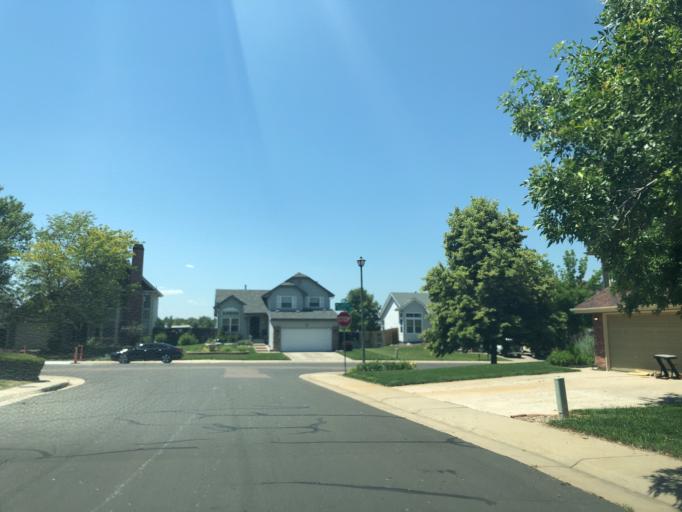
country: US
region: Colorado
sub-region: Arapahoe County
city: Dove Valley
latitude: 39.6296
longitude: -104.7759
